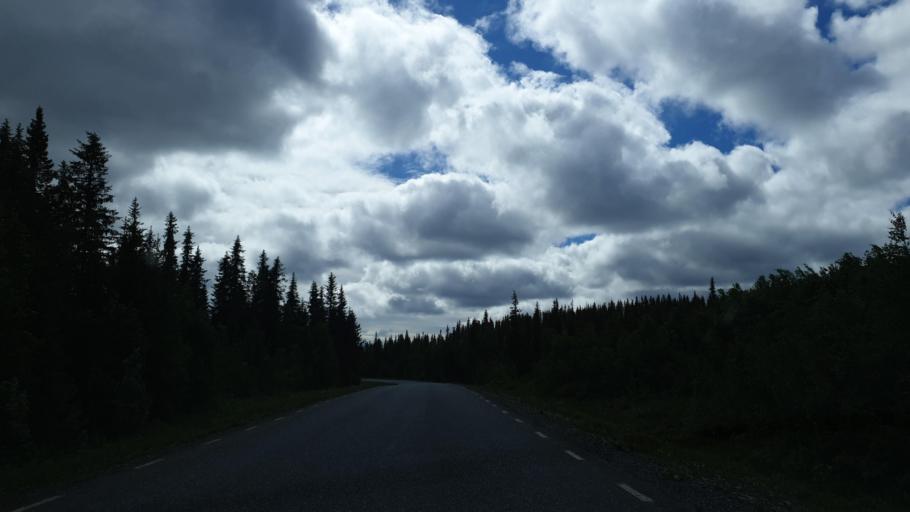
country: SE
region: Vaesterbotten
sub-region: Vilhelmina Kommun
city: Sjoberg
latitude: 65.2011
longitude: 15.9776
